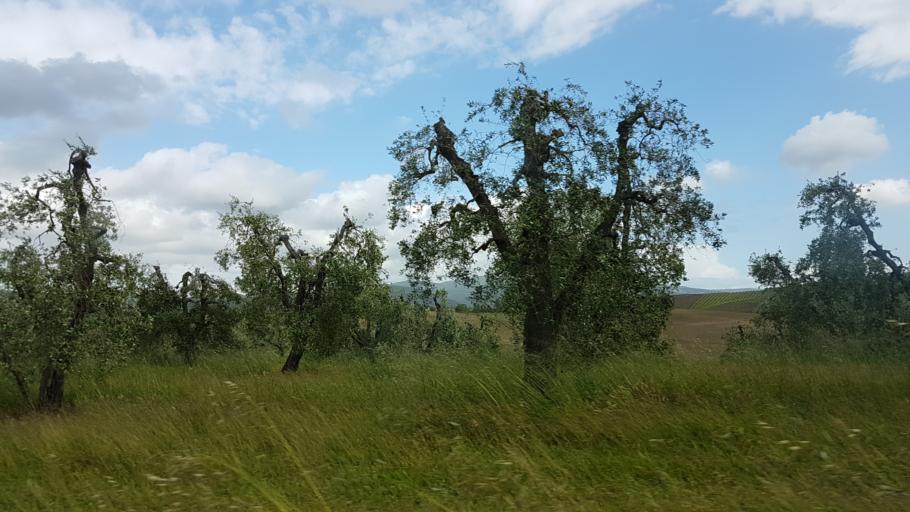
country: IT
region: Tuscany
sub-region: Province of Pisa
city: Santa Luce
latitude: 43.4645
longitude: 10.5404
